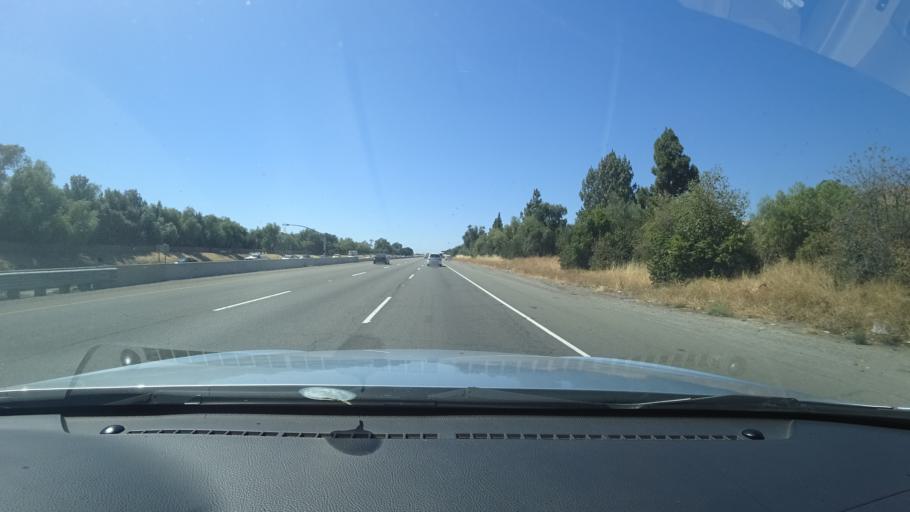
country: US
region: California
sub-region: Santa Clara County
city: Milpitas
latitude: 37.4582
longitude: -121.8985
